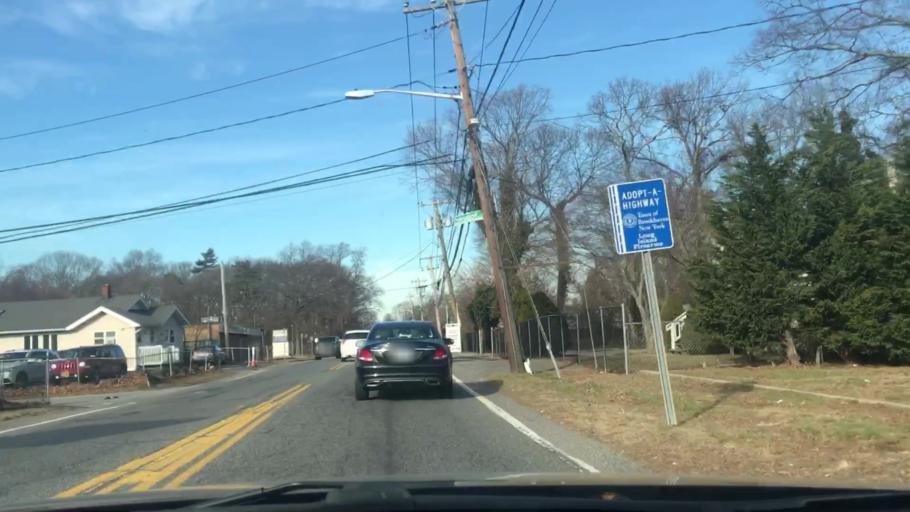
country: US
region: New York
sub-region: Suffolk County
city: Ronkonkoma
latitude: 40.8175
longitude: -73.1126
